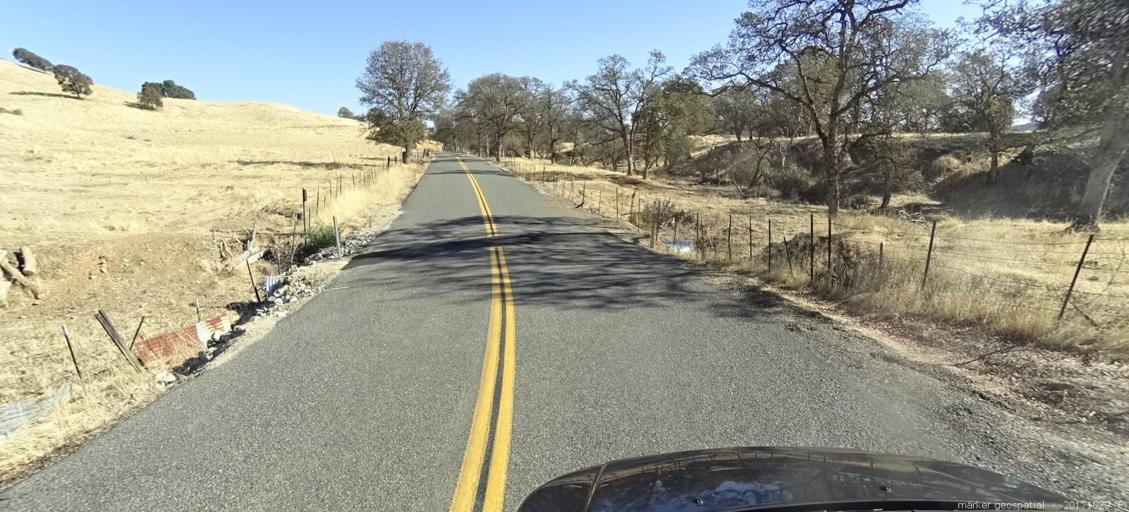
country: US
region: California
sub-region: Shasta County
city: Shasta
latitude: 40.4488
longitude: -122.6410
